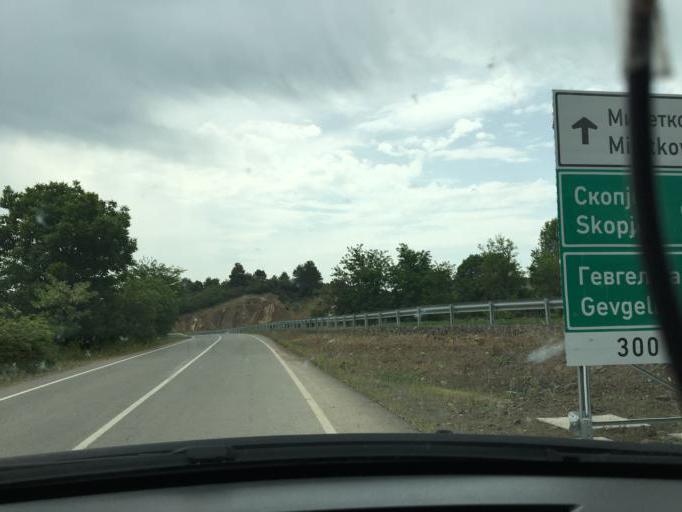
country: MK
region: Gevgelija
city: Miravci
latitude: 41.3054
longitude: 22.4421
